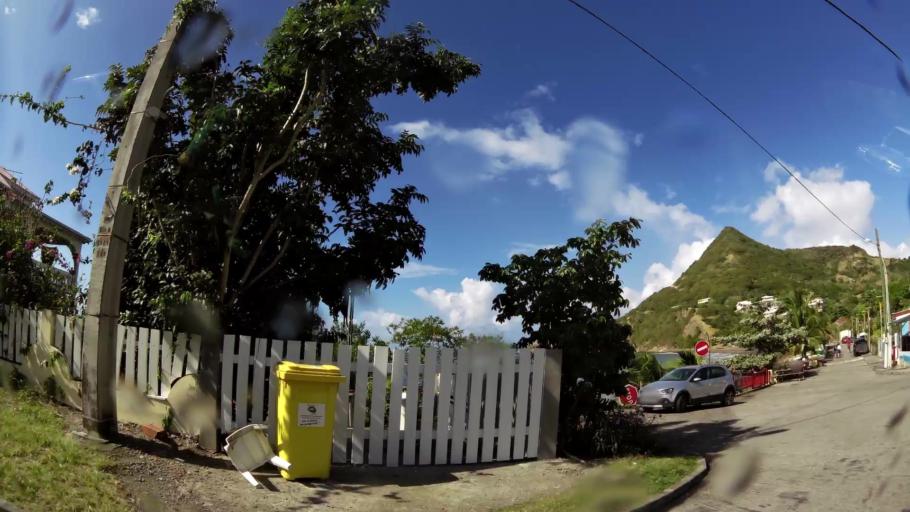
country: MQ
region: Martinique
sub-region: Martinique
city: Les Trois-Ilets
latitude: 14.4684
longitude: -61.0695
